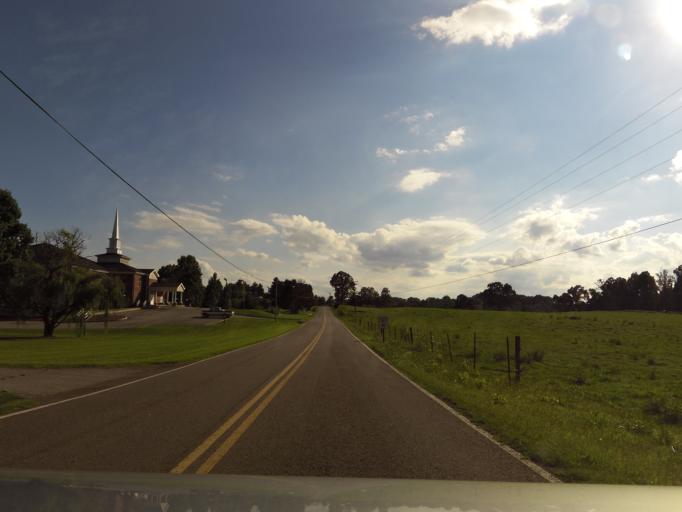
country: US
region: Tennessee
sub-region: Blount County
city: Maryville
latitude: 35.6938
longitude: -84.0345
